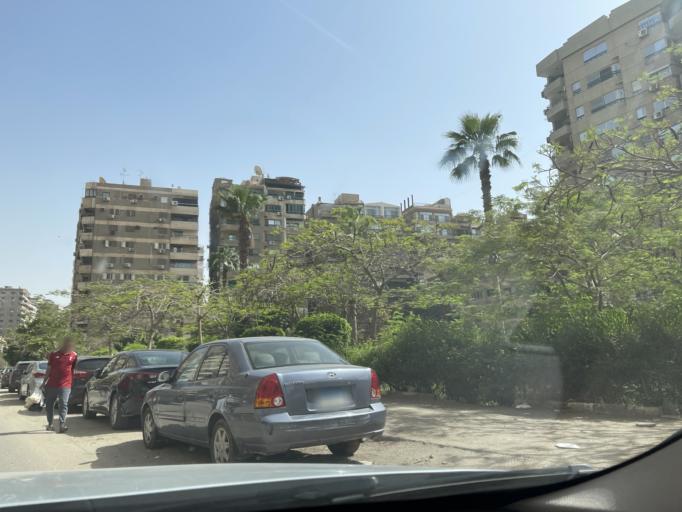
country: EG
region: Muhafazat al Qahirah
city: Cairo
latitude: 30.0672
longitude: 31.3560
